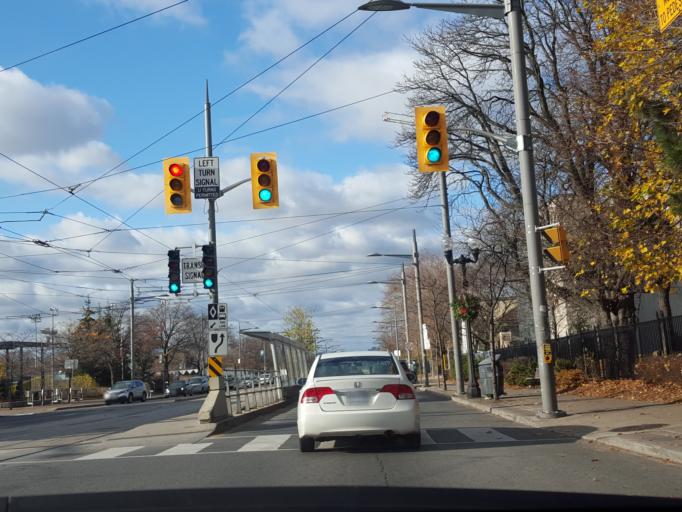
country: CA
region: Ontario
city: Toronto
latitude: 43.6764
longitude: -79.4505
